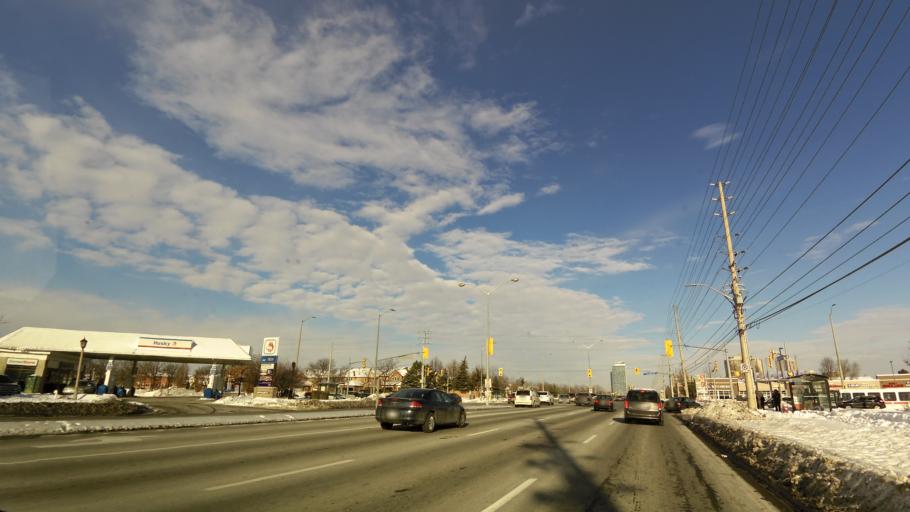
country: CA
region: Ontario
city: Mississauga
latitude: 43.5967
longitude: -79.6642
